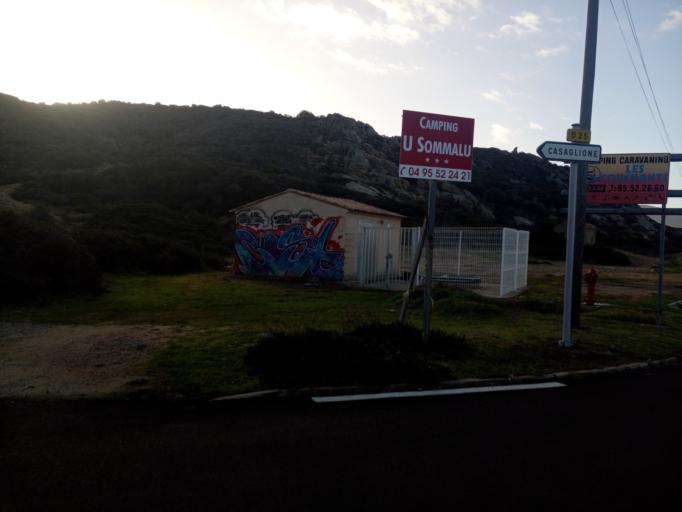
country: FR
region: Corsica
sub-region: Departement de la Corse-du-Sud
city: Appietto
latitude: 42.0697
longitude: 8.7223
